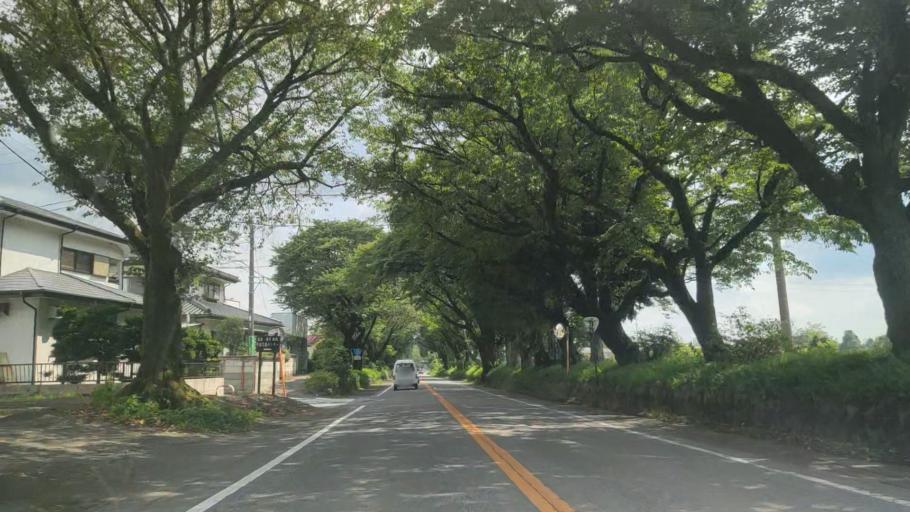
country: JP
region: Tochigi
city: Utsunomiya-shi
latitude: 36.6440
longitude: 139.8470
